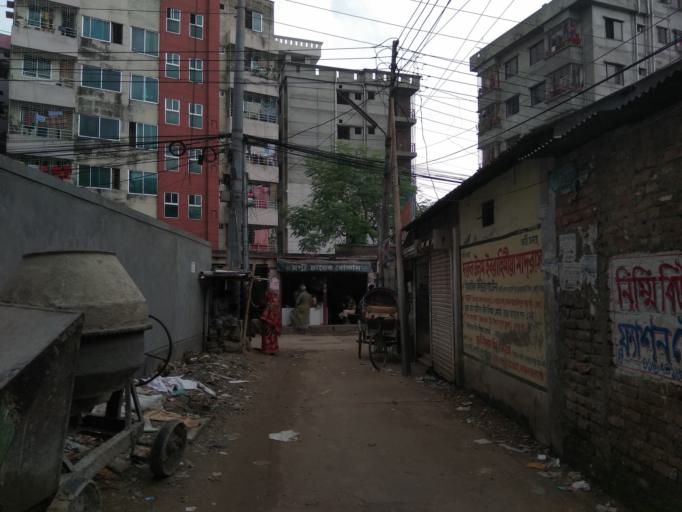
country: BD
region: Dhaka
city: Azimpur
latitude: 23.7984
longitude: 90.3770
